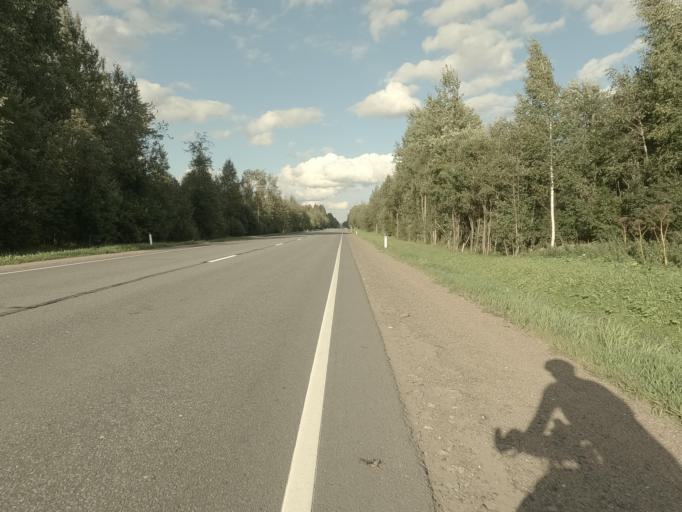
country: RU
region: Leningrad
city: Mga
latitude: 59.6852
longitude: 30.9606
